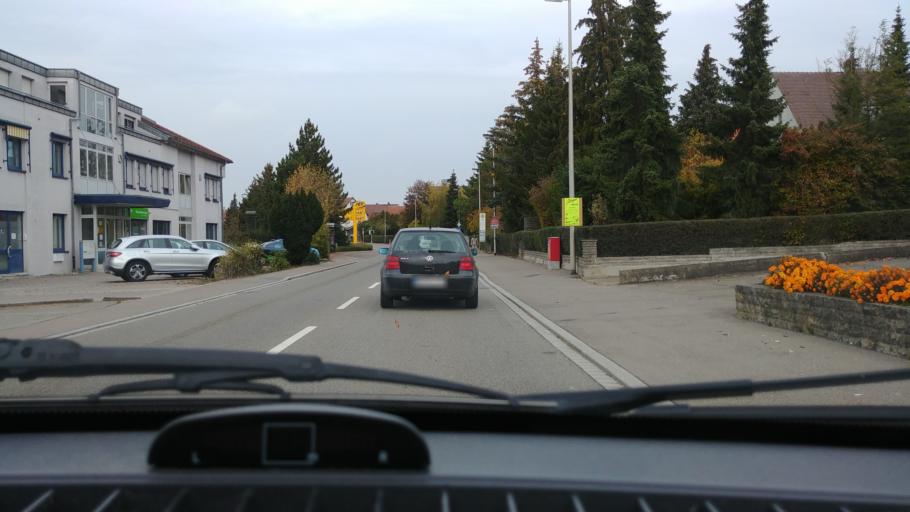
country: DE
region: Baden-Wuerttemberg
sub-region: Regierungsbezirk Stuttgart
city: Crailsheim
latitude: 49.1296
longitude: 10.0783
